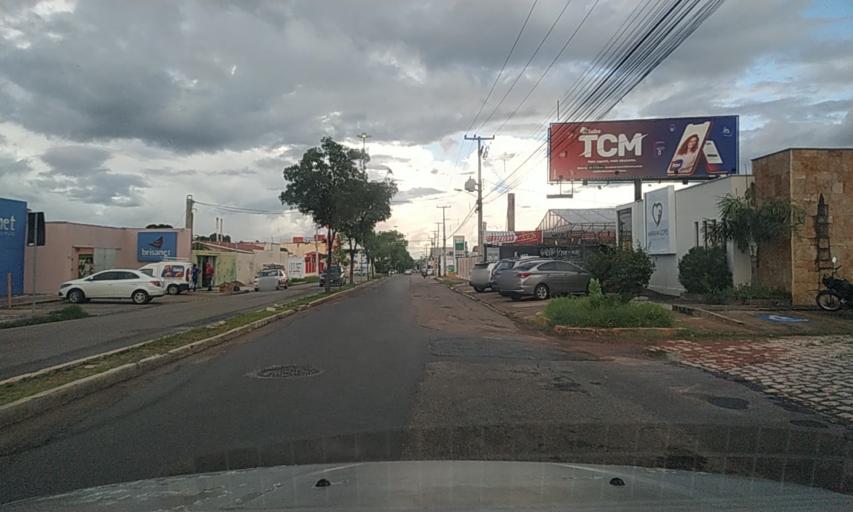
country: BR
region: Rio Grande do Norte
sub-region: Mossoro
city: Mossoro
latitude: -5.1817
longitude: -37.3610
